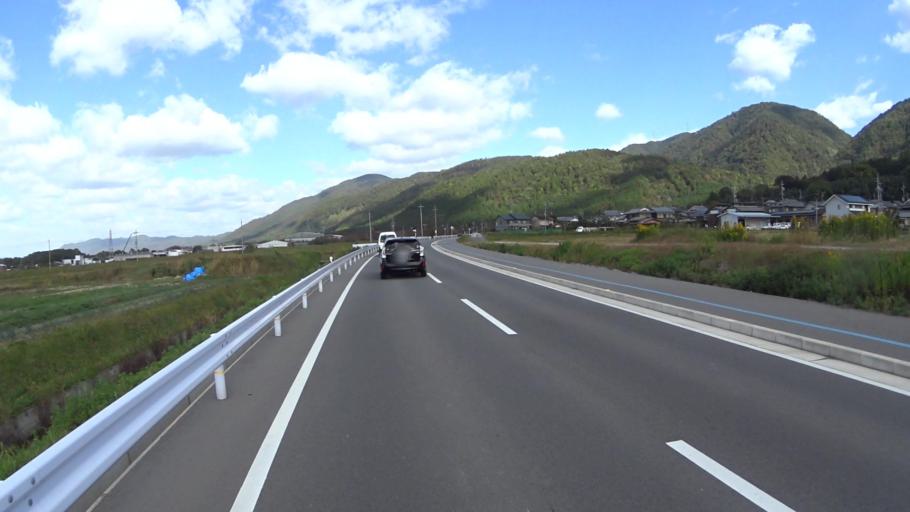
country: JP
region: Kyoto
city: Kameoka
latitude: 35.0397
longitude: 135.5823
